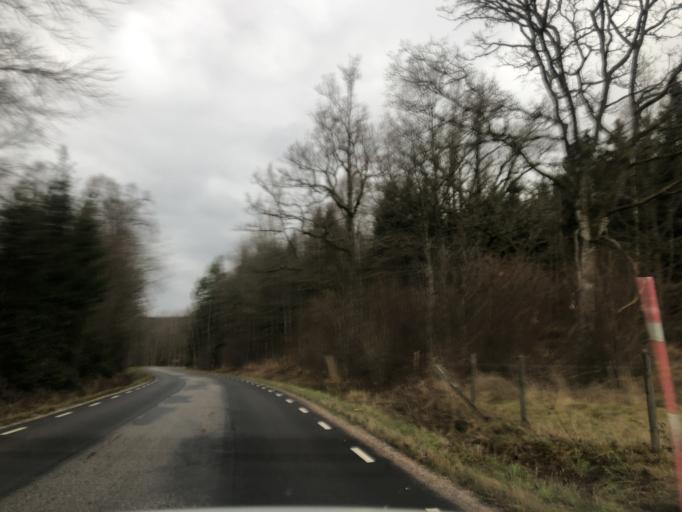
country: SE
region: Vaestra Goetaland
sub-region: Boras Kommun
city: Dalsjofors
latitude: 57.8237
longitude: 13.1930
